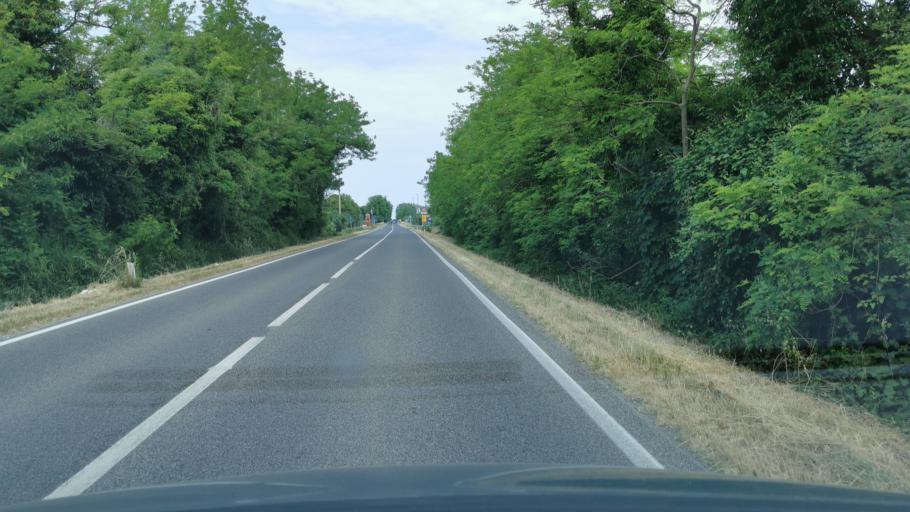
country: IT
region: Emilia-Romagna
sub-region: Provincia di Ravenna
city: Savarna-Conventella
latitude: 44.5322
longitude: 12.1221
